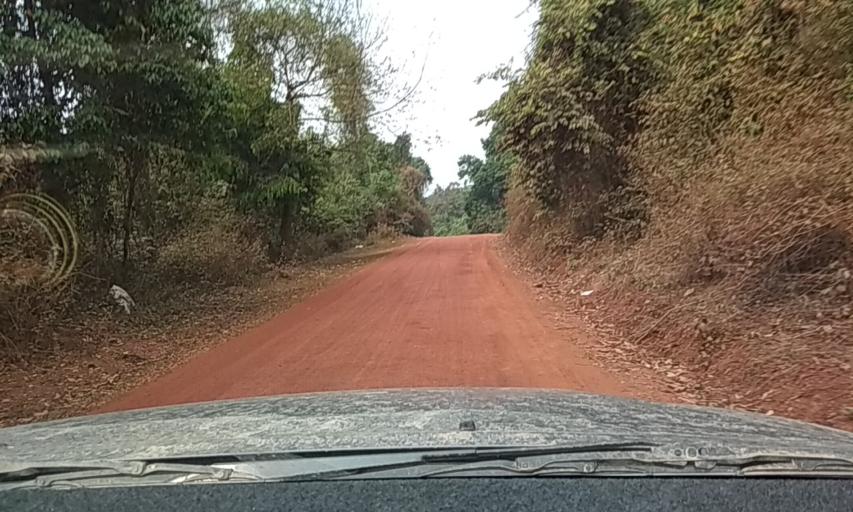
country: TH
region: Nan
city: Mae Charim
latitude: 18.4108
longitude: 101.1735
